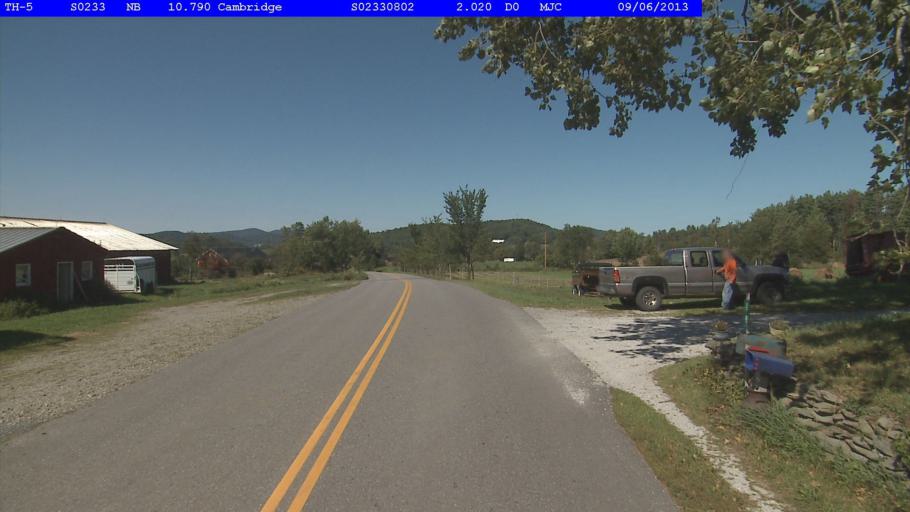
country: US
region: Vermont
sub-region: Chittenden County
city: Jericho
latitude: 44.6109
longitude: -72.8565
